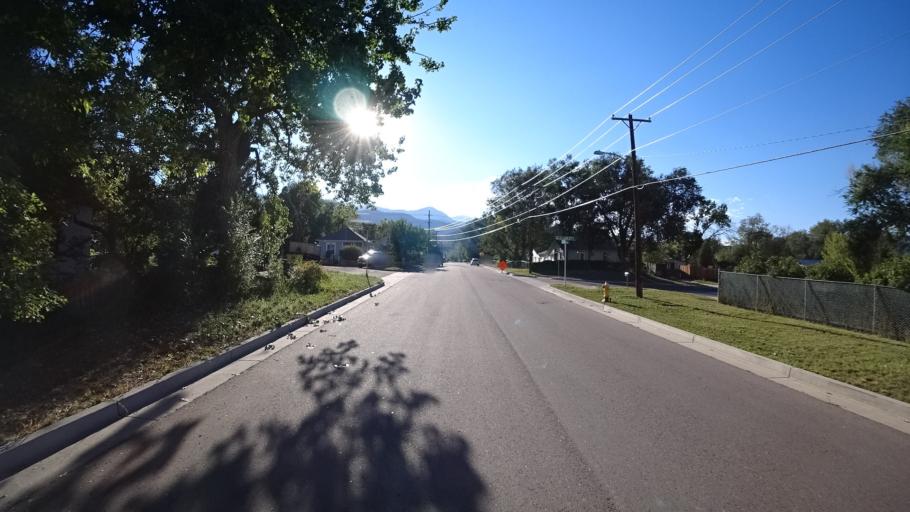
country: US
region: Colorado
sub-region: El Paso County
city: Colorado Springs
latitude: 38.8354
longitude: -104.8641
